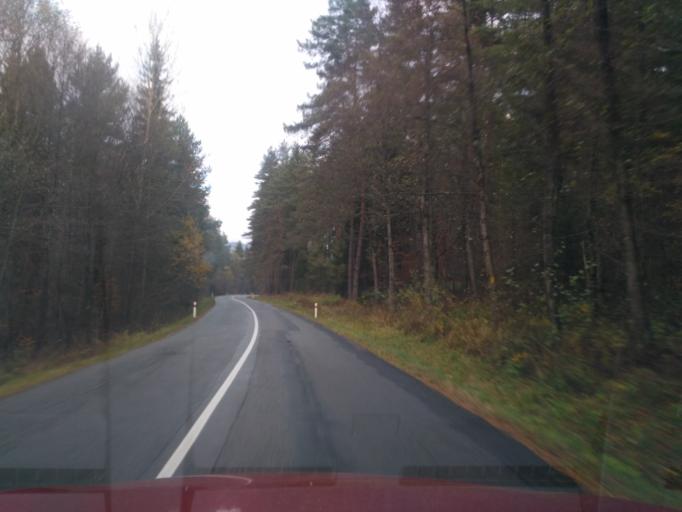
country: SK
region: Kosicky
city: Medzev
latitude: 48.7926
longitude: 20.7818
